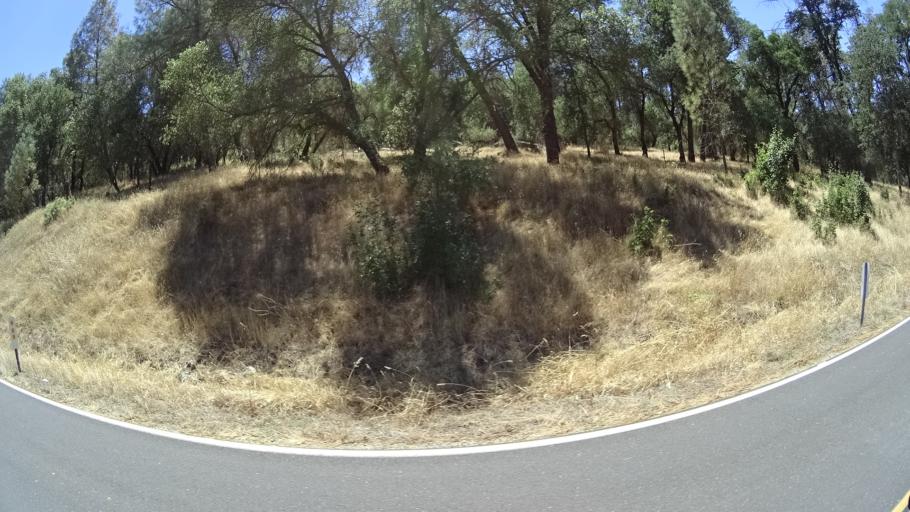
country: US
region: California
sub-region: Calaveras County
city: San Andreas
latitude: 38.1537
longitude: -120.6633
